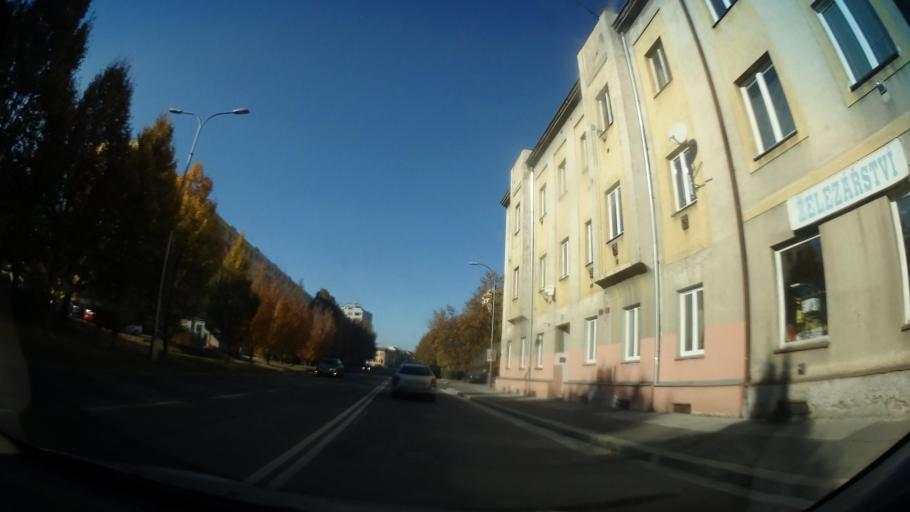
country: CZ
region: Pardubicky
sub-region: Okres Chrudim
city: Chrudim
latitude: 49.9455
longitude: 15.7947
